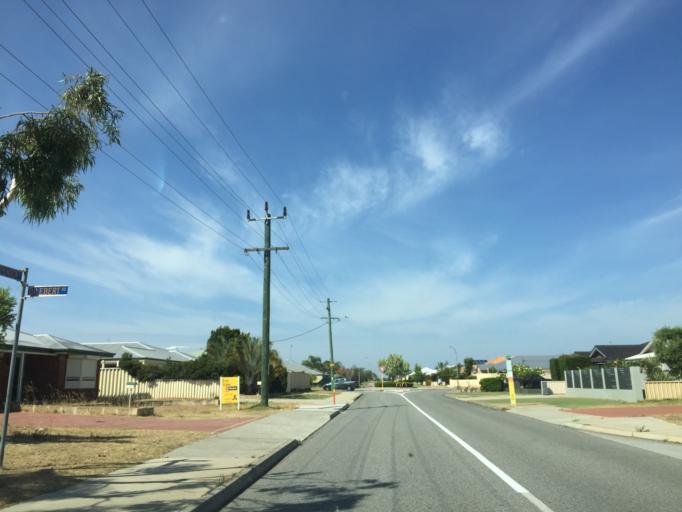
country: AU
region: Western Australia
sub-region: Gosnells
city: Southern River
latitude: -32.0842
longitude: 115.9580
